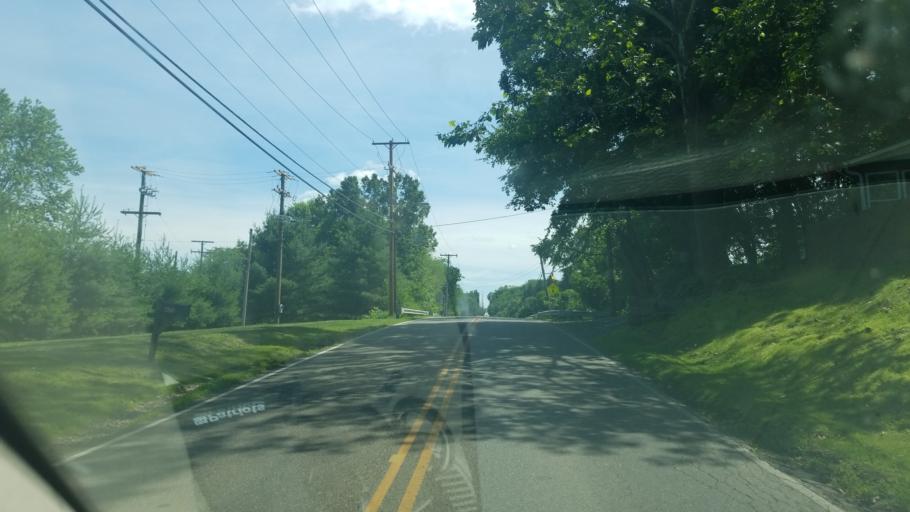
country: US
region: Ohio
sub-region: Stark County
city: Massillon
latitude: 40.8025
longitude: -81.5436
